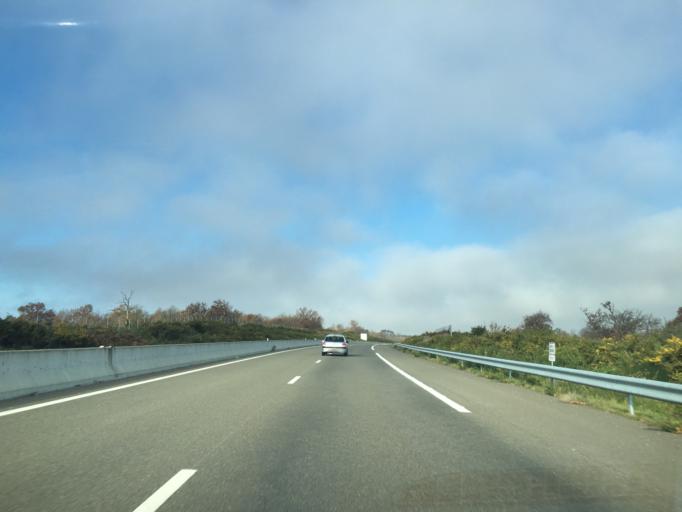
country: FR
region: Aquitaine
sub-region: Departement des Landes
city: Villeneuve-de-Marsan
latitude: 43.8007
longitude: -0.3006
